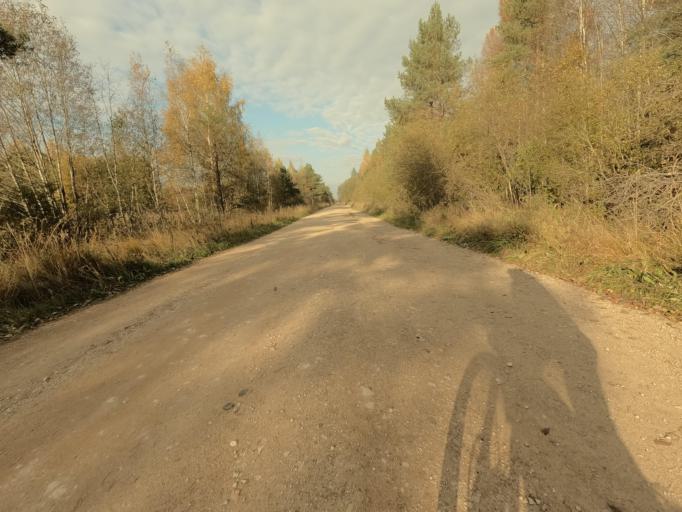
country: RU
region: Novgorod
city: Volkhovskiy
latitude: 58.8970
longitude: 31.0307
